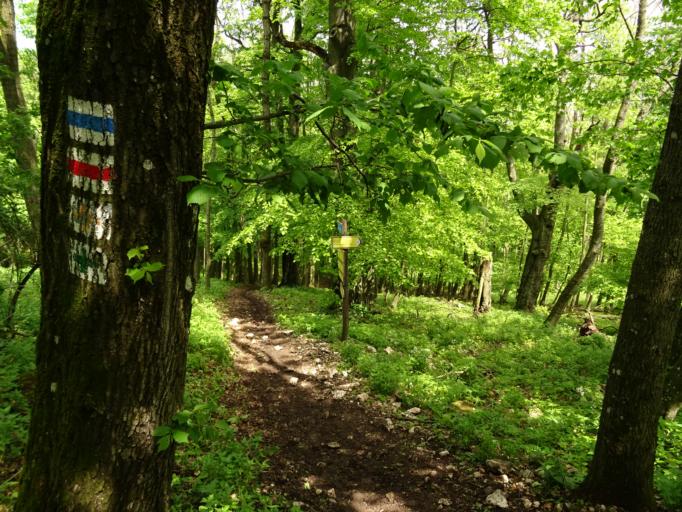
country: HU
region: Gyor-Moson-Sopron
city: Bakonyszentlaszlo
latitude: 47.2945
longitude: 17.7548
